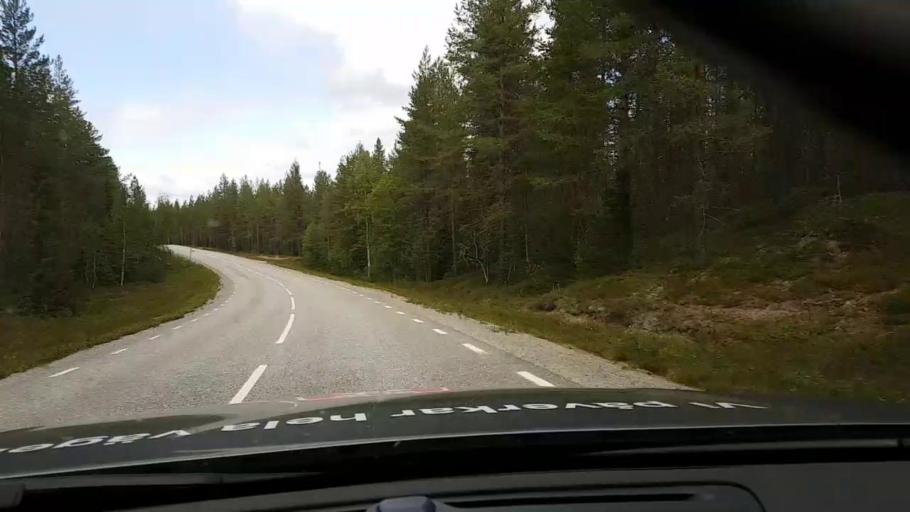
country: SE
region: Vaesternorrland
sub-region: OErnskoeldsviks Kommun
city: Bredbyn
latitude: 63.7024
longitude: 17.7634
